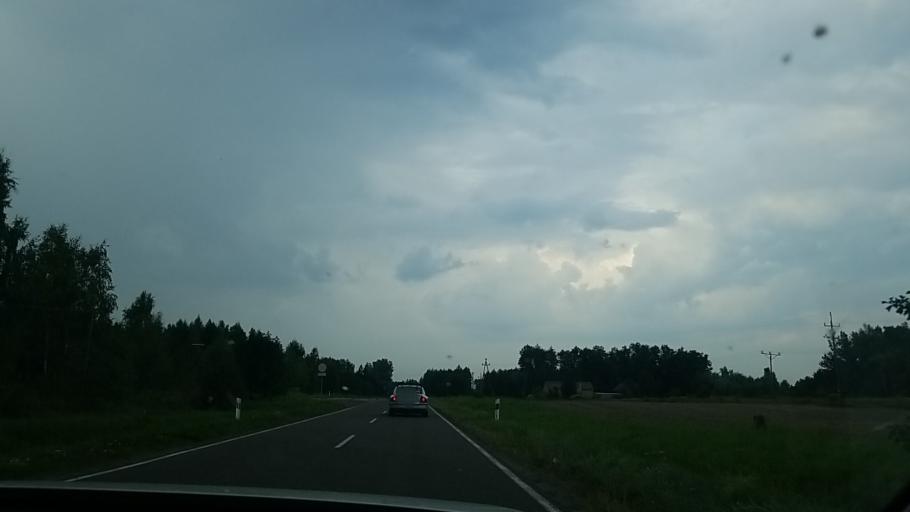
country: PL
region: Lublin Voivodeship
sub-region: Powiat leczynski
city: Cycow
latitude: 51.2800
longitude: 23.0999
